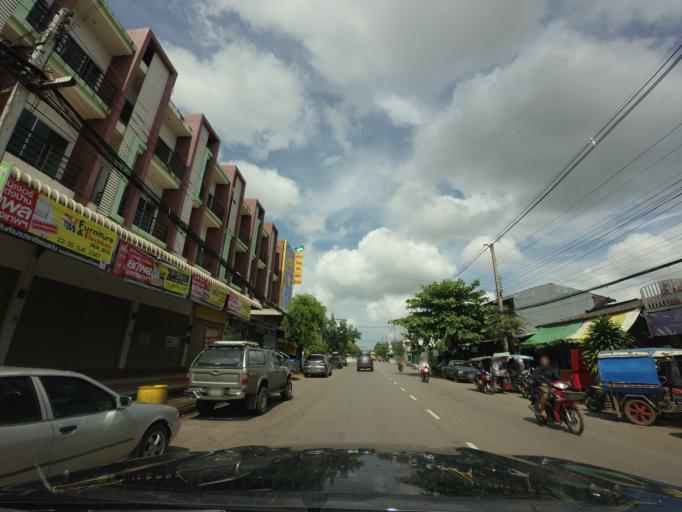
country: TH
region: Changwat Udon Thani
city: Udon Thani
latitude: 17.4018
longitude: 102.7872
